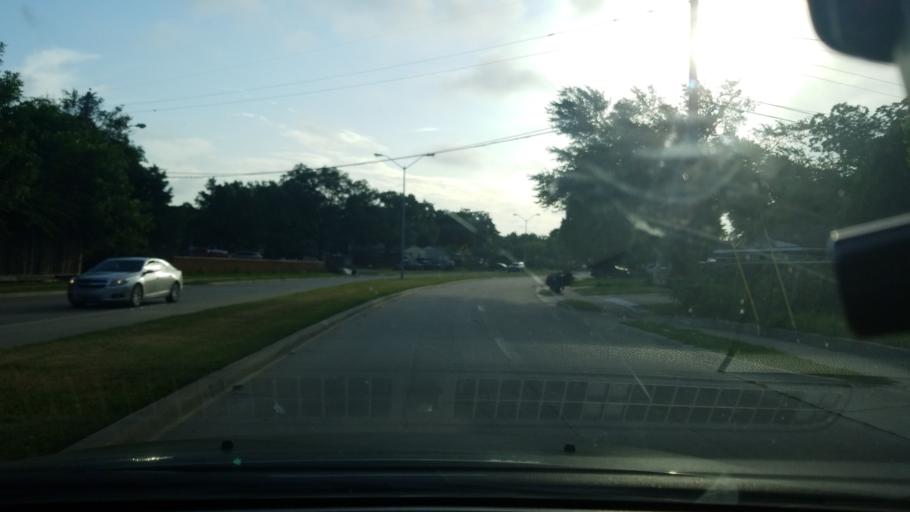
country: US
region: Texas
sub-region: Dallas County
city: Mesquite
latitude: 32.8271
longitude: -96.6603
